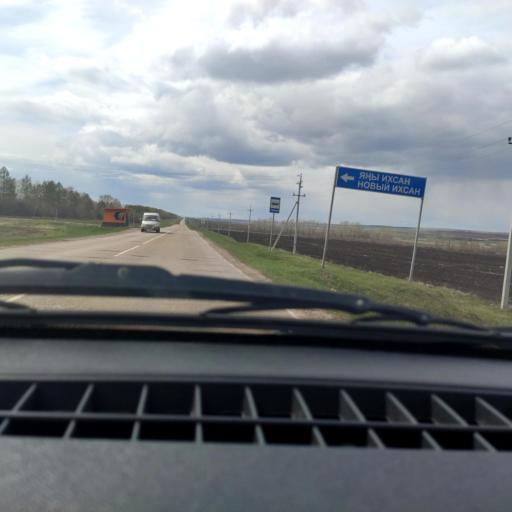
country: RU
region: Bashkortostan
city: Chekmagush
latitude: 55.1092
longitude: 54.9475
